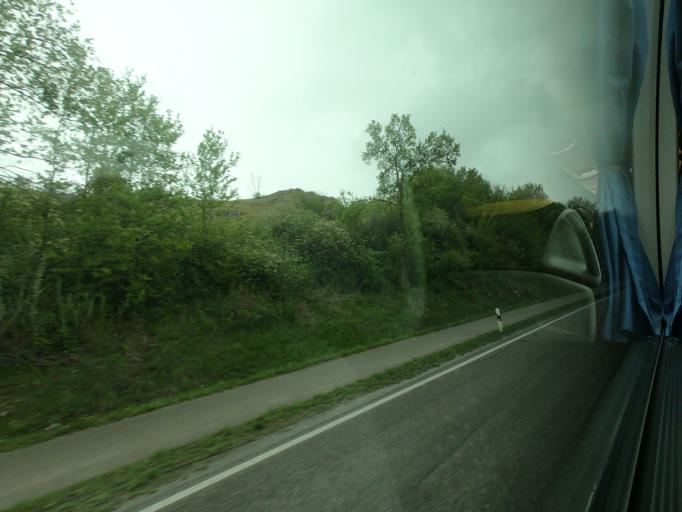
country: DE
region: Baden-Wuerttemberg
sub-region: Regierungsbezirk Stuttgart
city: Heidenheim an der Brenz
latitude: 48.7240
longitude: 10.1575
